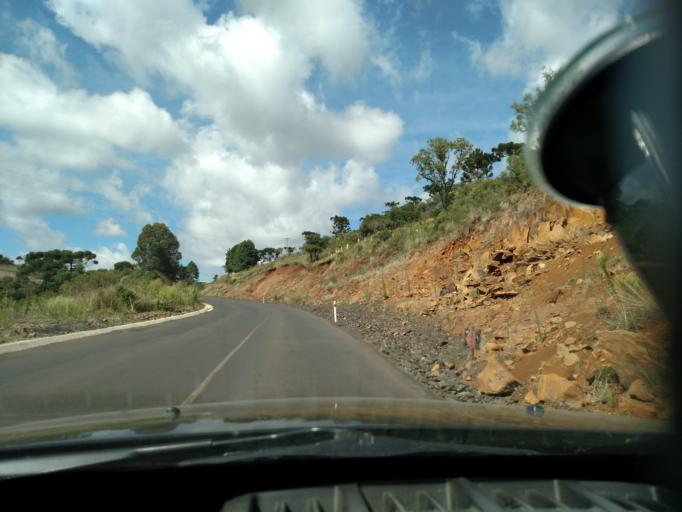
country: BR
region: Santa Catarina
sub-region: Sao Joaquim
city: Sao Joaquim
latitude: -28.1037
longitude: -50.0521
